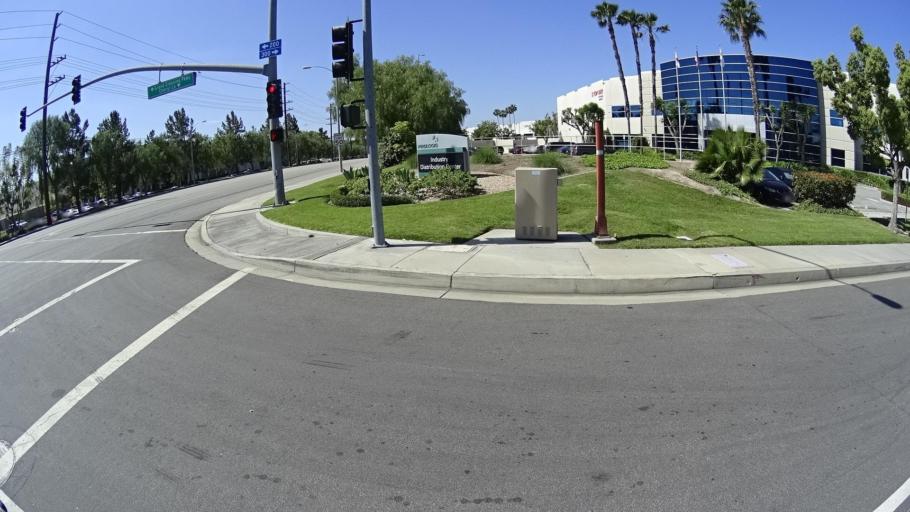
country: US
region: California
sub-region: Los Angeles County
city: Walnut
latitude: 34.0150
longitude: -117.8431
